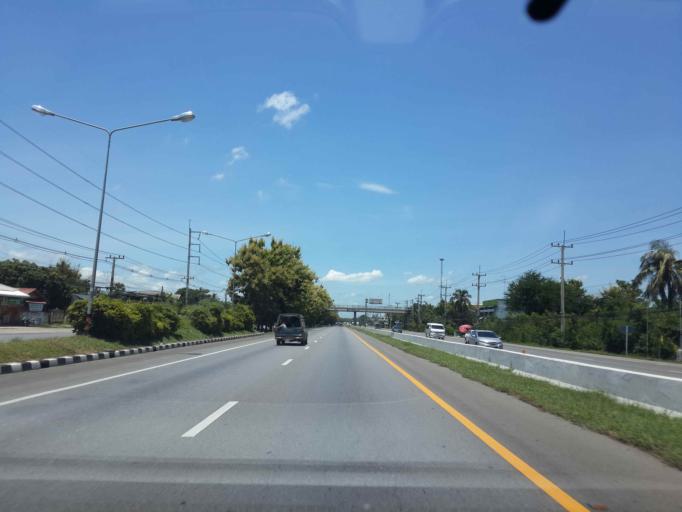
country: TH
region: Phetchaburi
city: Khao Yoi
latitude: 13.1938
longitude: 99.8318
